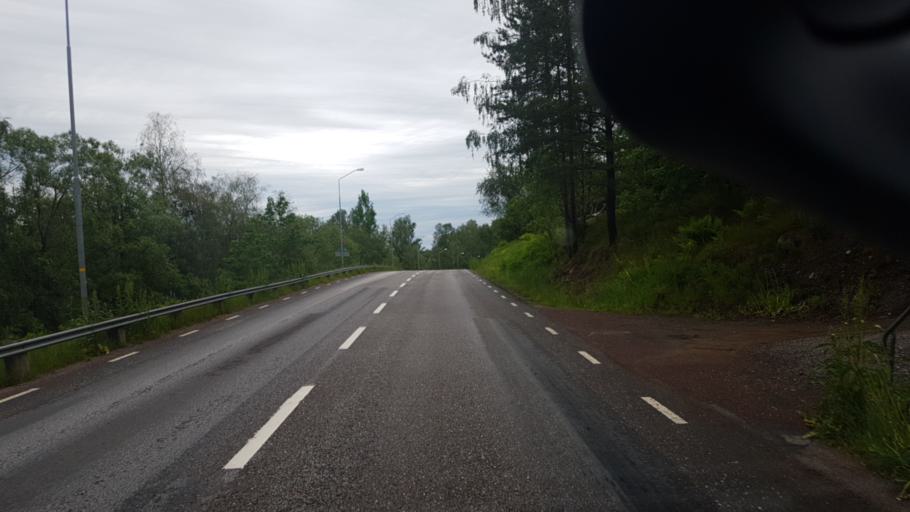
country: SE
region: Vaermland
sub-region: Eda Kommun
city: Amotfors
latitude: 59.7123
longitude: 12.1551
